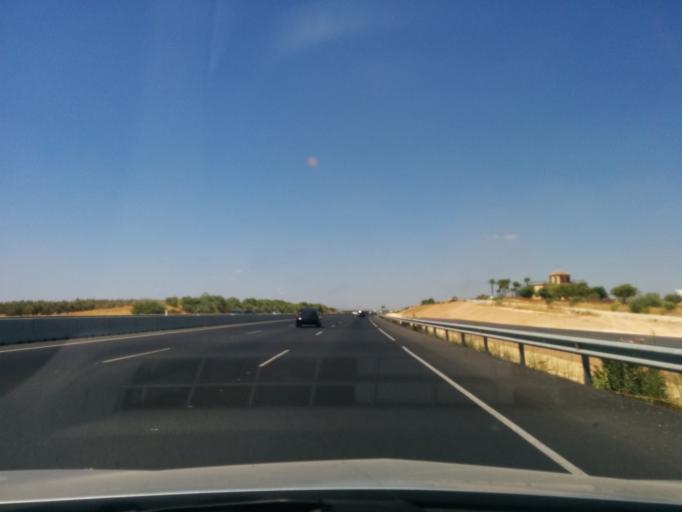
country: ES
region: Andalusia
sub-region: Provincia de Sevilla
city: Espartinas
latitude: 37.3649
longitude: -6.1181
